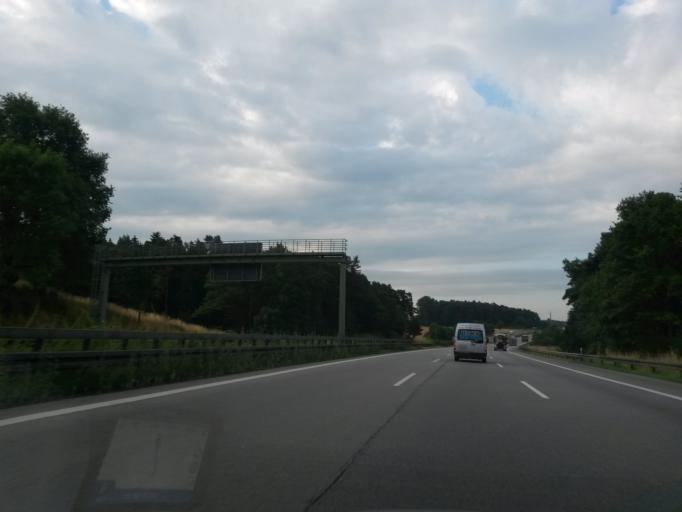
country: DE
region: Bavaria
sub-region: Upper Bavaria
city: Rohrbach
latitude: 48.6335
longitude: 11.5233
